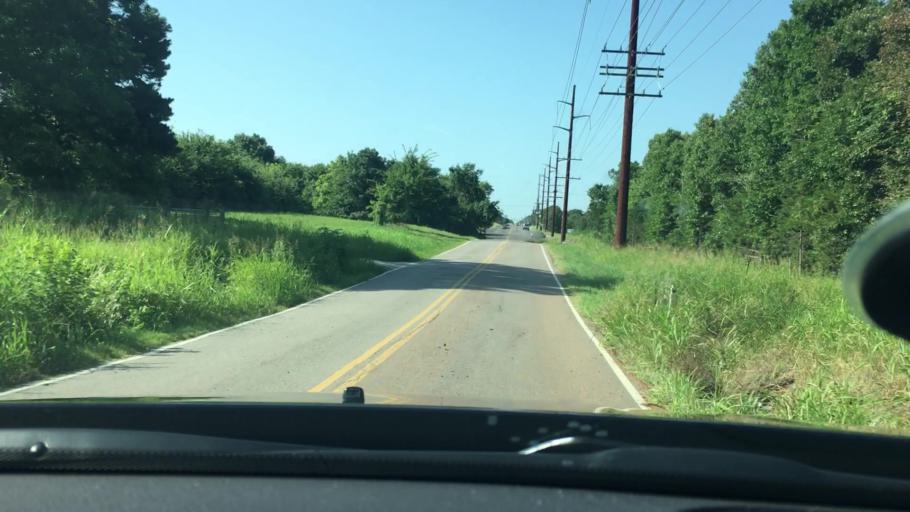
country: US
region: Oklahoma
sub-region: Pontotoc County
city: Ada
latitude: 34.7927
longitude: -96.6348
